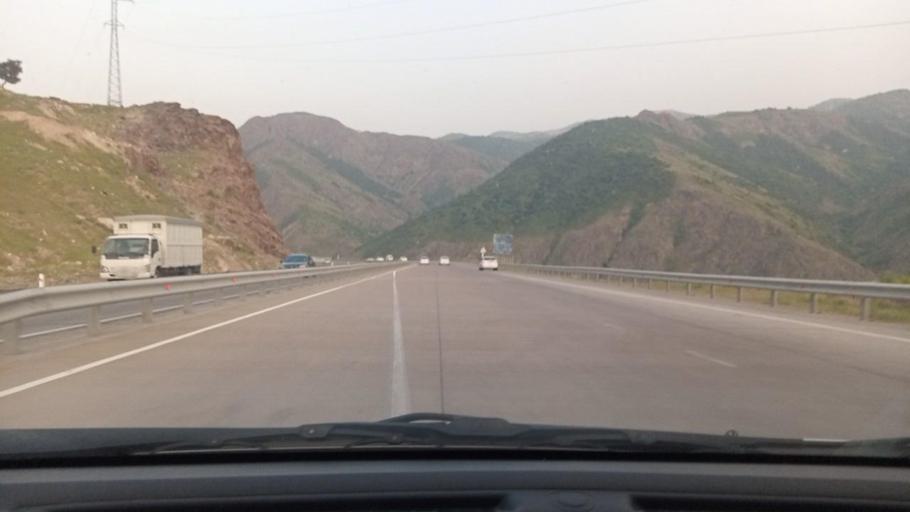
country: UZ
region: Toshkent
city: Angren
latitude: 41.0734
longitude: 70.2687
